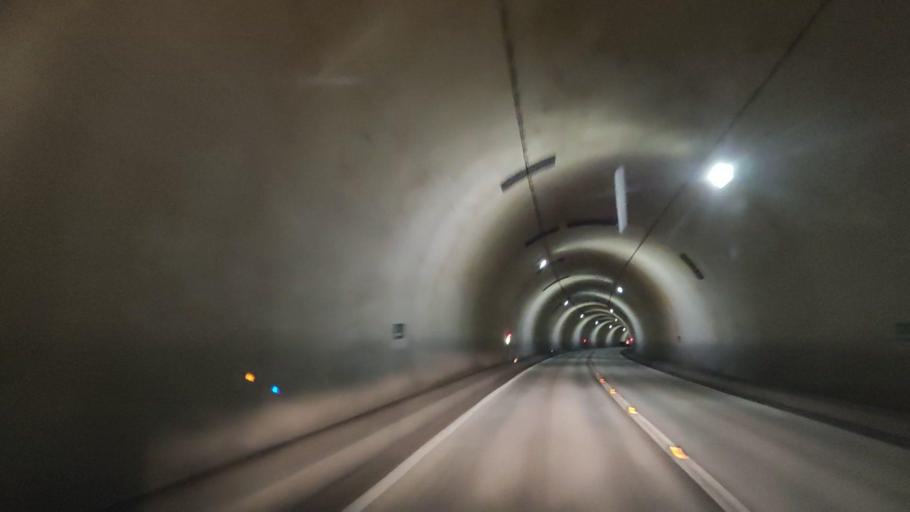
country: JP
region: Tottori
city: Yonago
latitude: 35.2680
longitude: 133.4354
